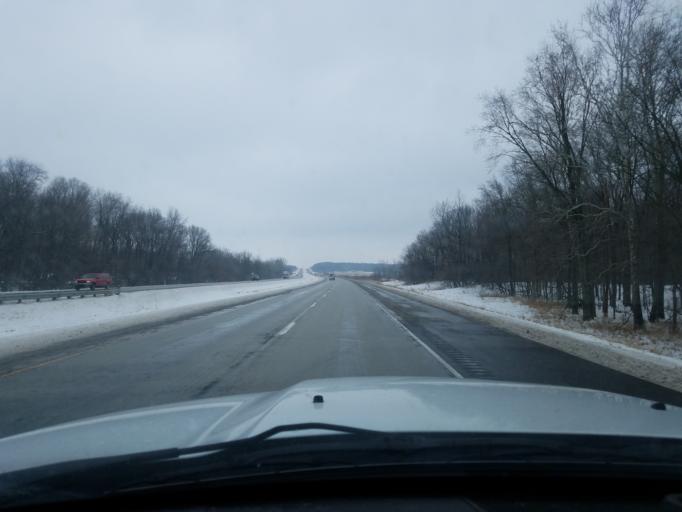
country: US
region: Indiana
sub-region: Fulton County
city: Rochester
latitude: 41.0953
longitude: -86.2400
